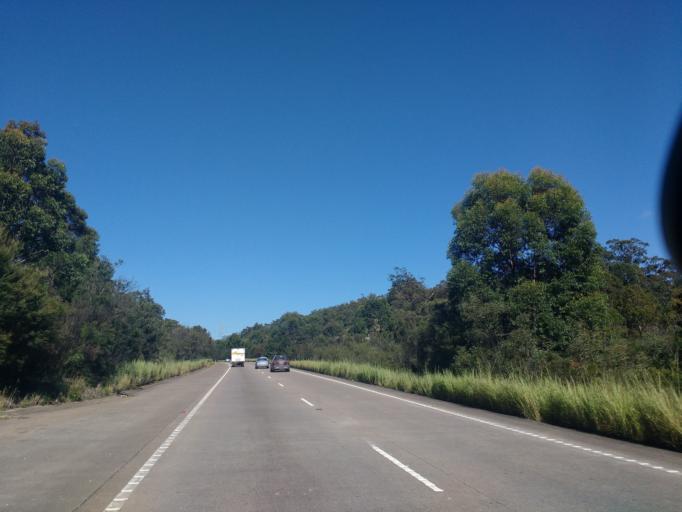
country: AU
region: New South Wales
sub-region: Lake Macquarie Shire
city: Holmesville
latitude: -32.9359
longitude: 151.5482
